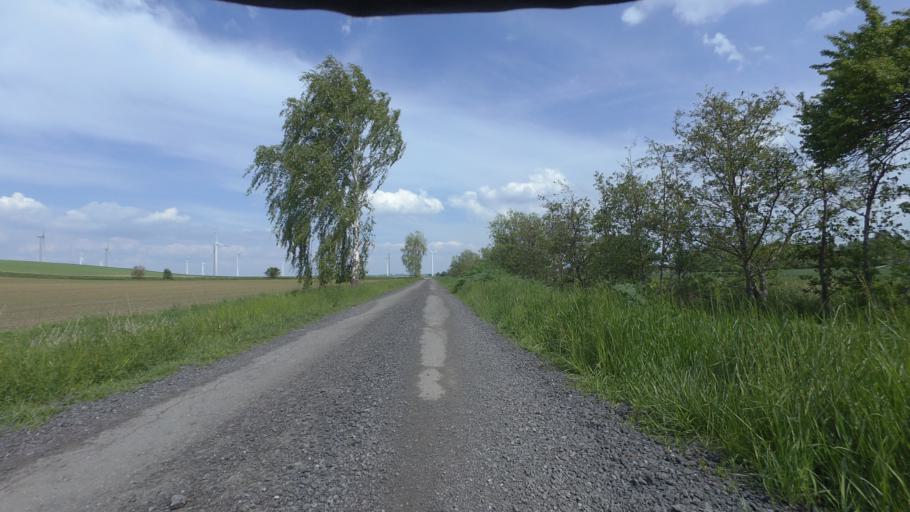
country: DE
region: Lower Saxony
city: Sollingen
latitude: 52.0664
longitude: 10.9274
